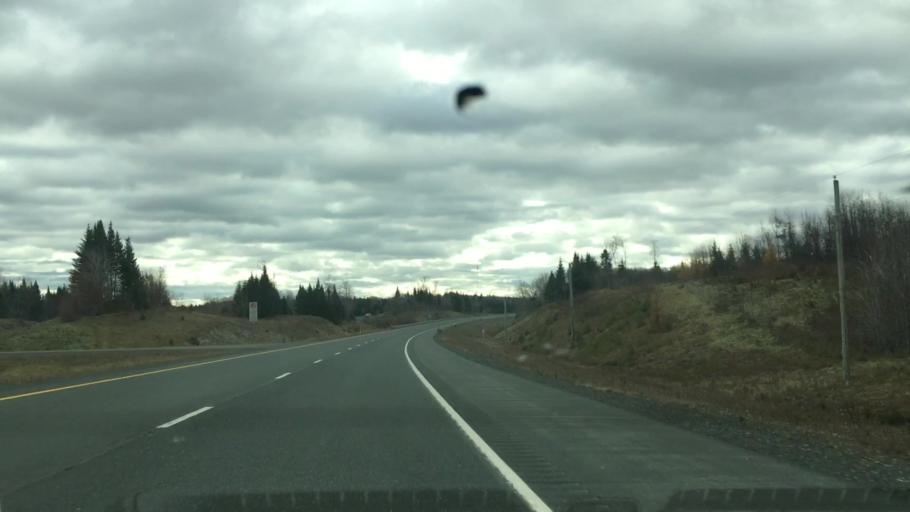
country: US
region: Maine
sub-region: Aroostook County
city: Easton
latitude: 46.6246
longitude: -67.7394
